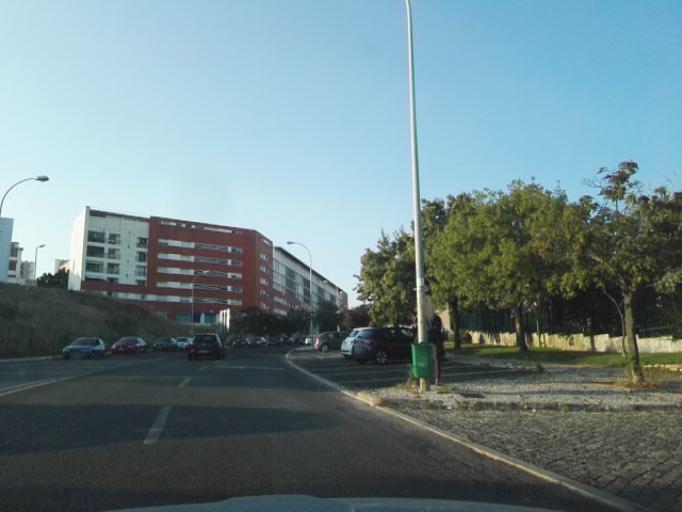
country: PT
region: Lisbon
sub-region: Amadora
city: Amadora
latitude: 38.7309
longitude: -9.2161
